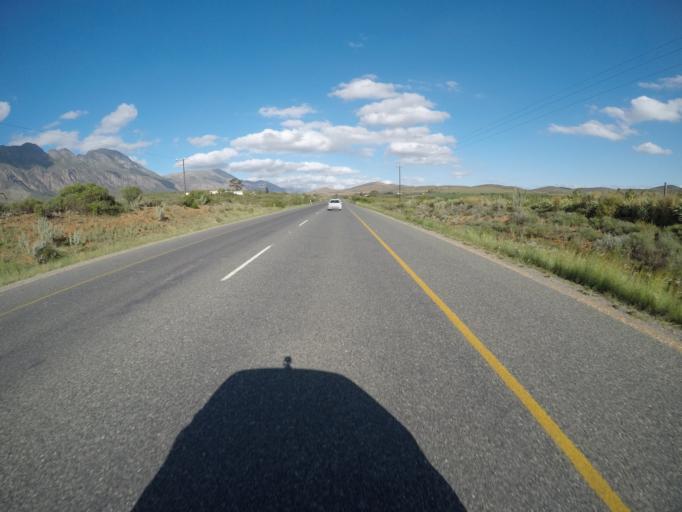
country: ZA
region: Western Cape
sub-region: Cape Winelands District Municipality
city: Ashton
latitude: -33.8544
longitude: 20.1052
